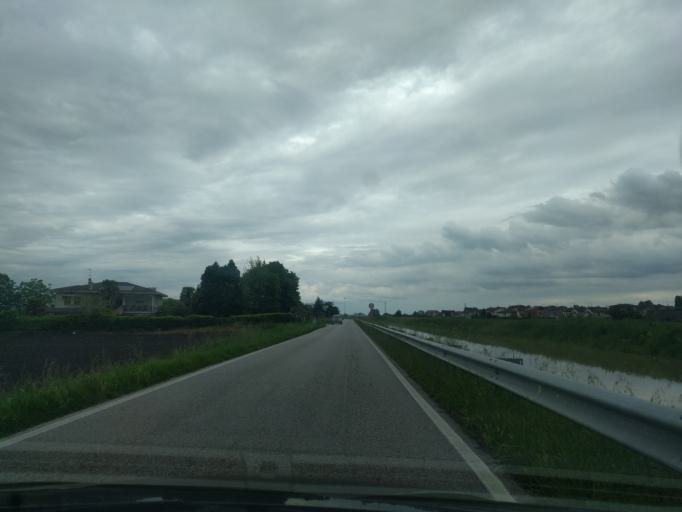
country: IT
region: Veneto
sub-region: Provincia di Rovigo
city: Rovigo
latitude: 45.0843
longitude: 11.7936
